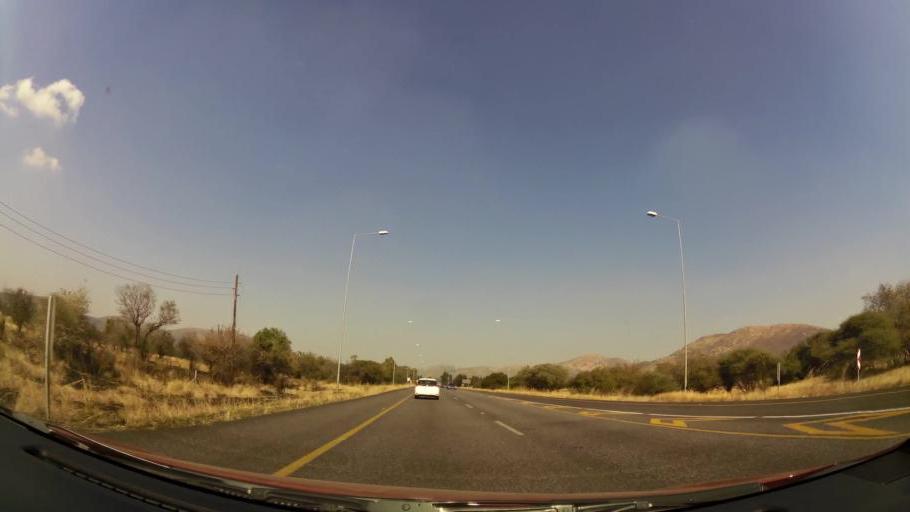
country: ZA
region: North-West
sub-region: Bojanala Platinum District Municipality
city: Rustenburg
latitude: -25.6198
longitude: 27.1556
